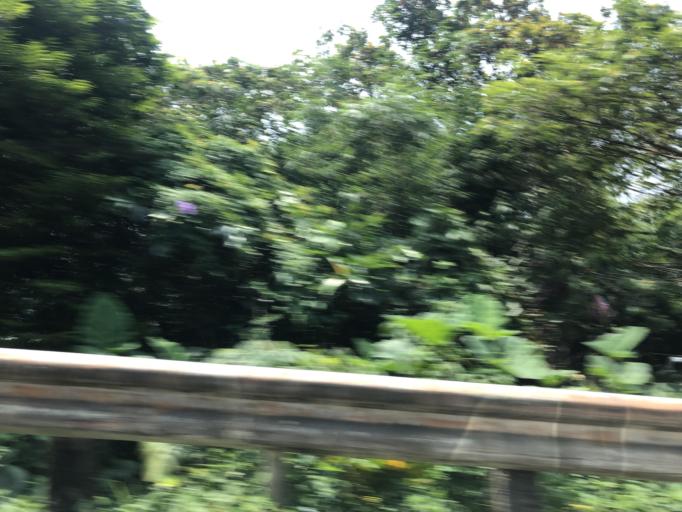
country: TW
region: Taiwan
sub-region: Keelung
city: Keelung
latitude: 25.1122
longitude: 121.7322
